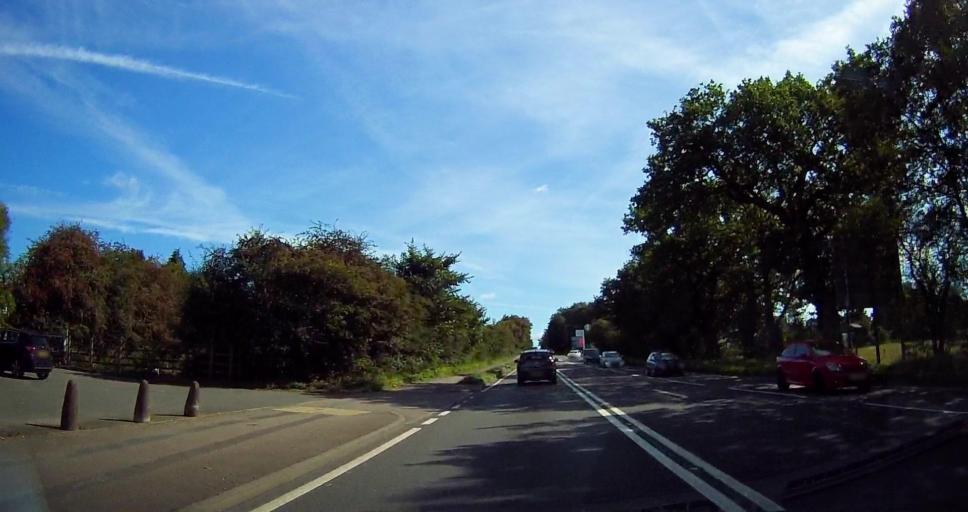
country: GB
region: England
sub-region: Staffordshire
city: Norton Canes
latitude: 52.6598
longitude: -1.9703
